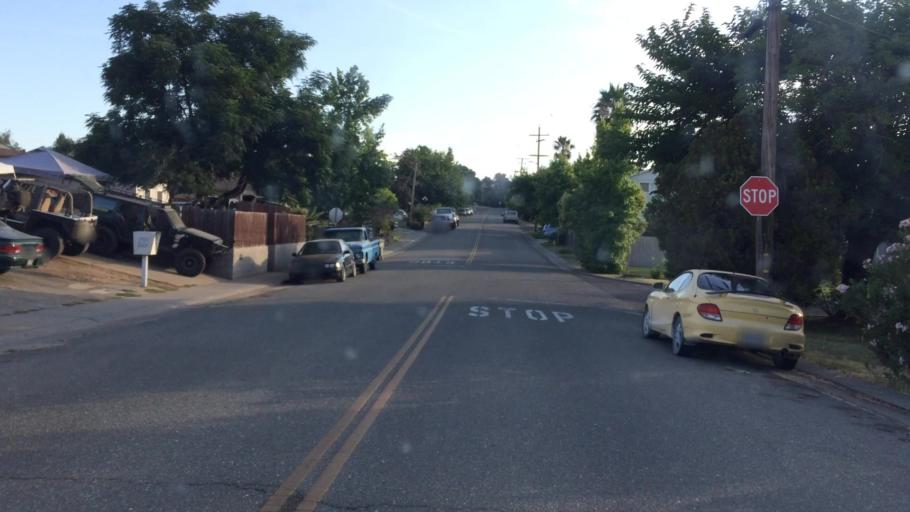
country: US
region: California
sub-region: Amador County
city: Ione
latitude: 38.3562
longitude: -120.9409
